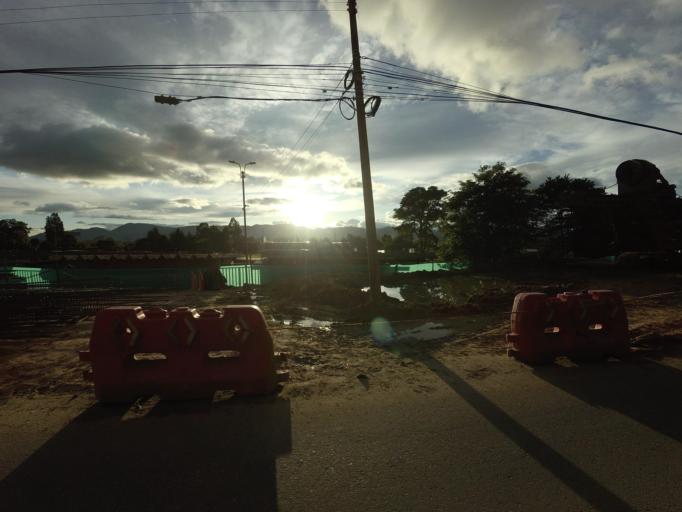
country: CO
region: Cundinamarca
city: Chia
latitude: 4.8276
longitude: -74.0308
